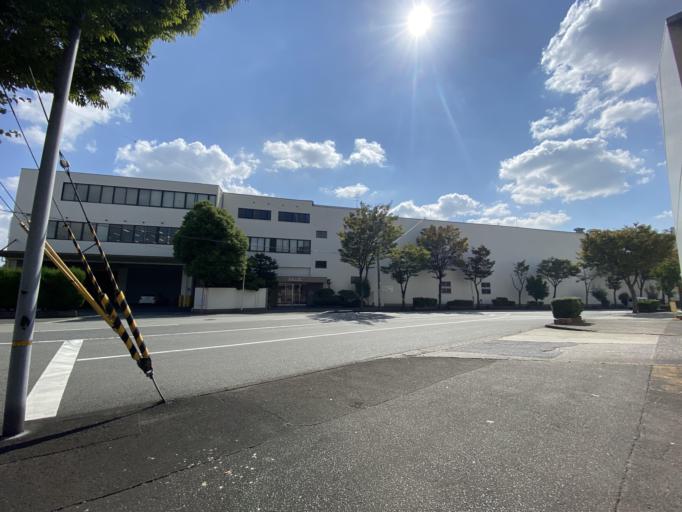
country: JP
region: Hyogo
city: Amagasaki
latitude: 34.7171
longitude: 135.4368
